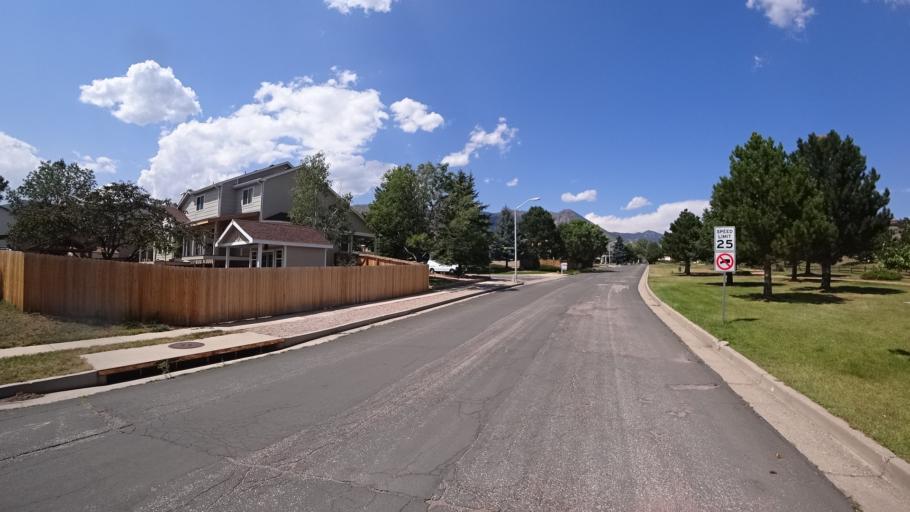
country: US
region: Colorado
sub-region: El Paso County
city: Air Force Academy
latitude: 38.9279
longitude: -104.8660
